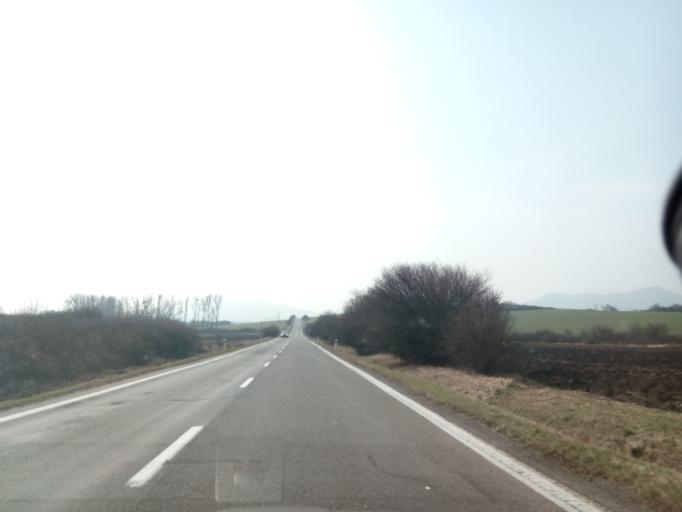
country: HU
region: Borsod-Abauj-Zemplen
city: Satoraljaujhely
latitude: 48.4942
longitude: 21.6498
